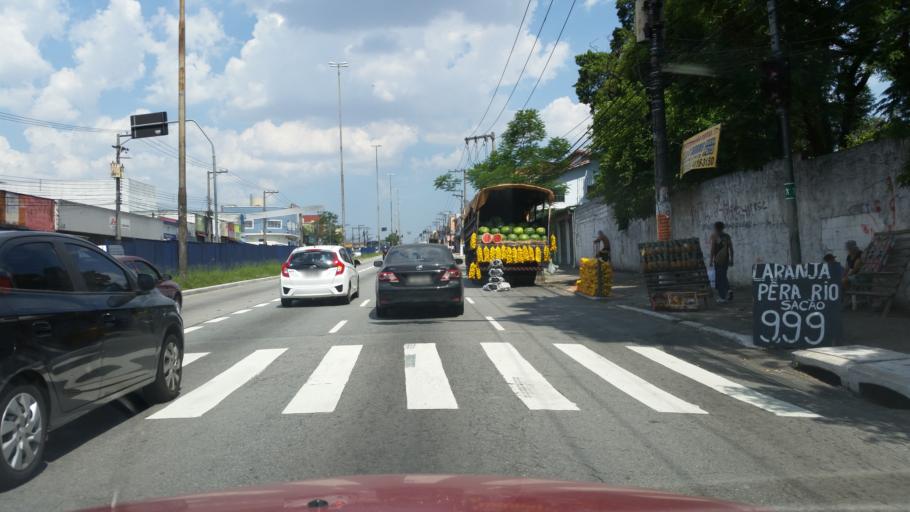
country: BR
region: Sao Paulo
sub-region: Diadema
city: Diadema
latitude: -23.6646
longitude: -46.6597
